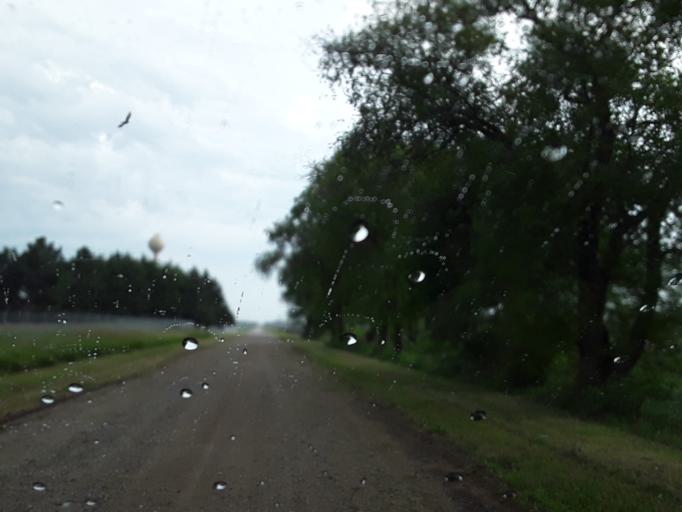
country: US
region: Nebraska
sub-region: Saunders County
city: Yutan
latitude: 41.1893
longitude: -96.4449
